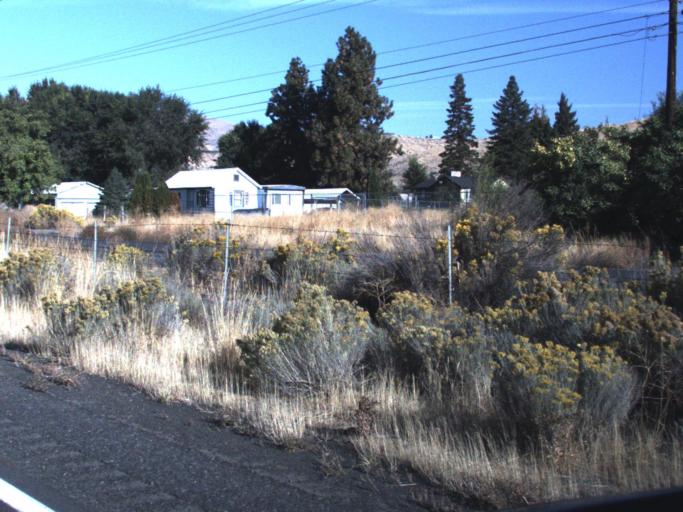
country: US
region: Washington
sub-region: Yakima County
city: Gleed
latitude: 46.7136
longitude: -120.6709
